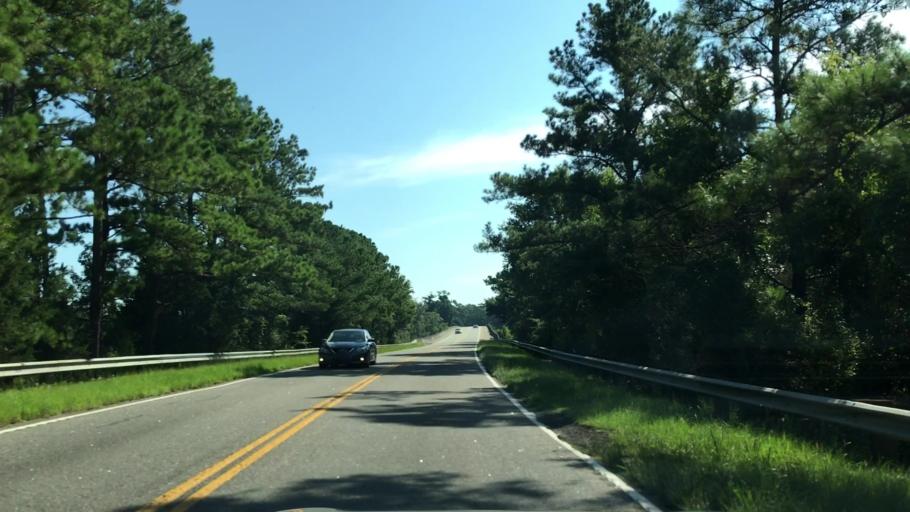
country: US
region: South Carolina
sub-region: Georgetown County
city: Georgetown
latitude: 33.4779
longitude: -79.2764
